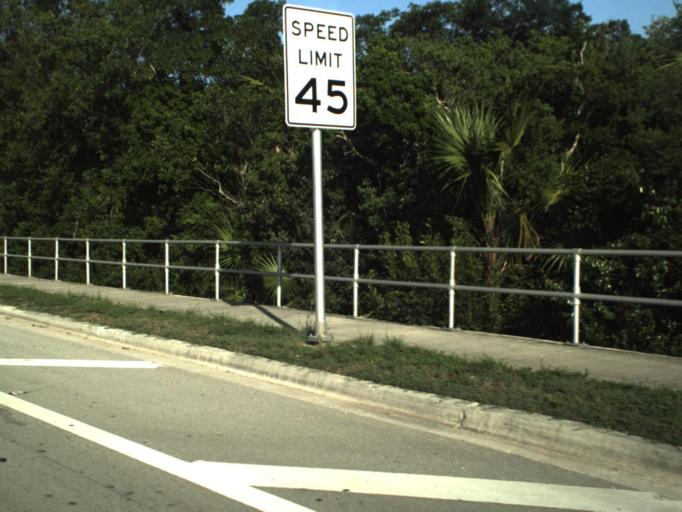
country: US
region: Florida
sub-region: Monroe County
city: Marathon
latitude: 24.7356
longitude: -81.0112
